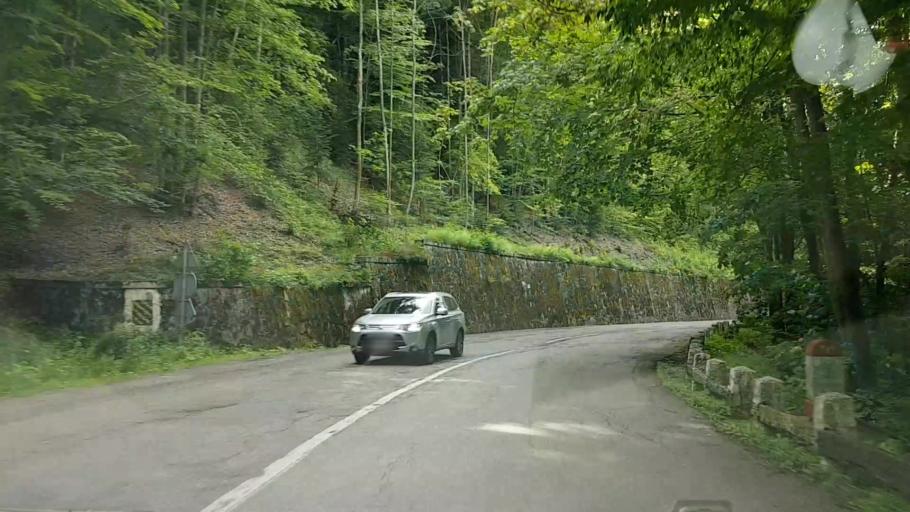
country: RO
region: Neamt
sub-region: Comuna Pangarati
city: Pangarati
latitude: 46.9348
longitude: 26.1215
